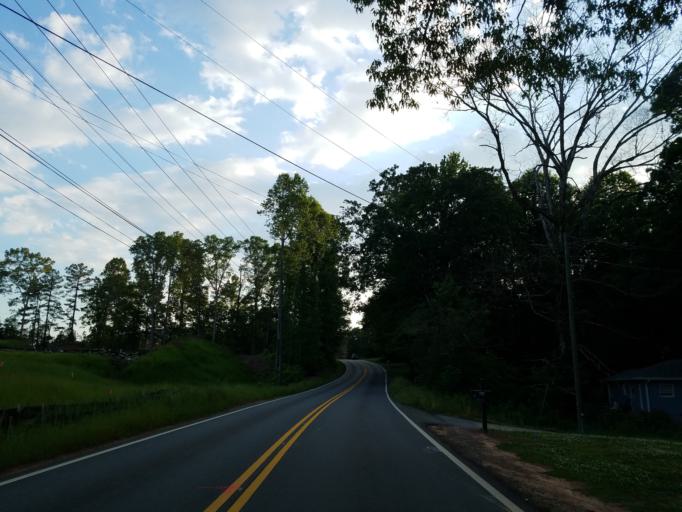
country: US
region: Georgia
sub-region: Cherokee County
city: Holly Springs
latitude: 34.1749
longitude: -84.5550
